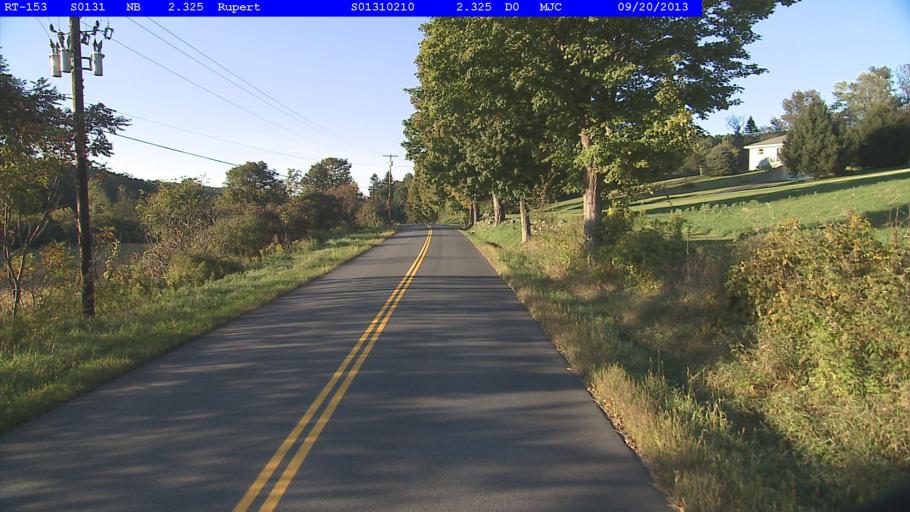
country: US
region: New York
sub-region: Washington County
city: Granville
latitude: 43.2885
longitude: -73.2391
